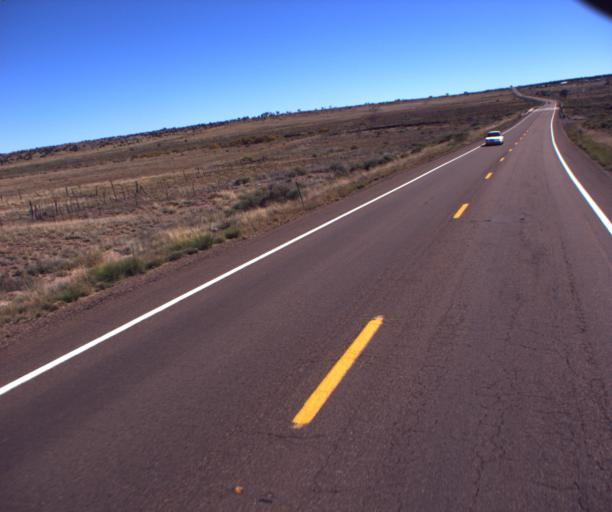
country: US
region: Arizona
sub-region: Apache County
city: Saint Johns
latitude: 34.5102
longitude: -109.4428
